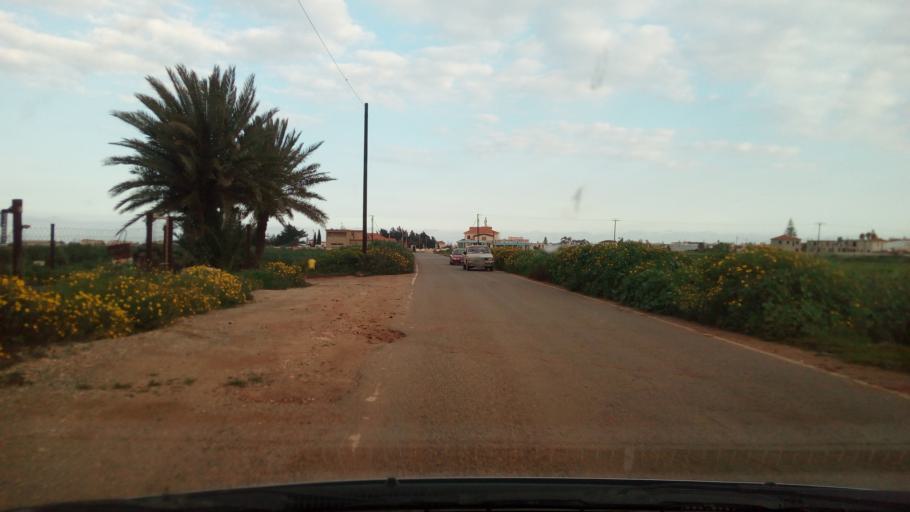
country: CY
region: Ammochostos
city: Avgorou
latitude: 34.9816
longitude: 33.8408
